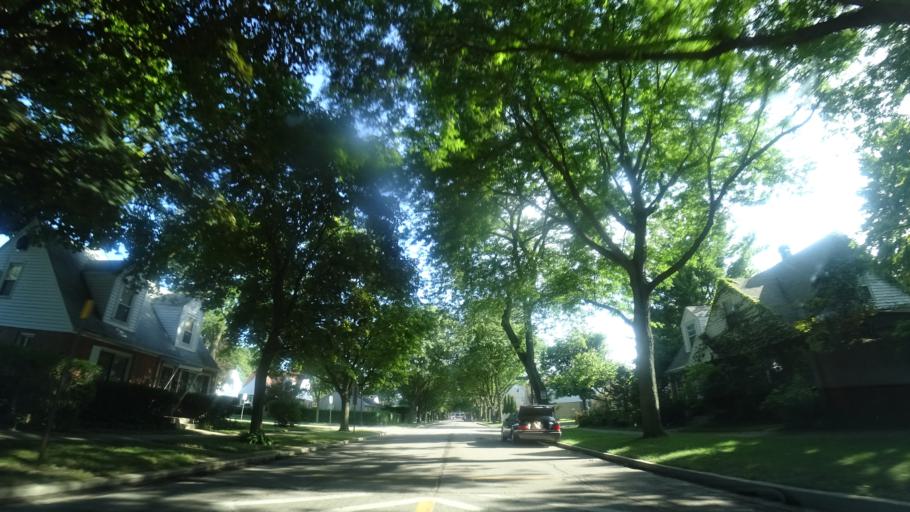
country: US
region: Illinois
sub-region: Cook County
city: Evanston
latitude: 42.0369
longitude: -87.7070
